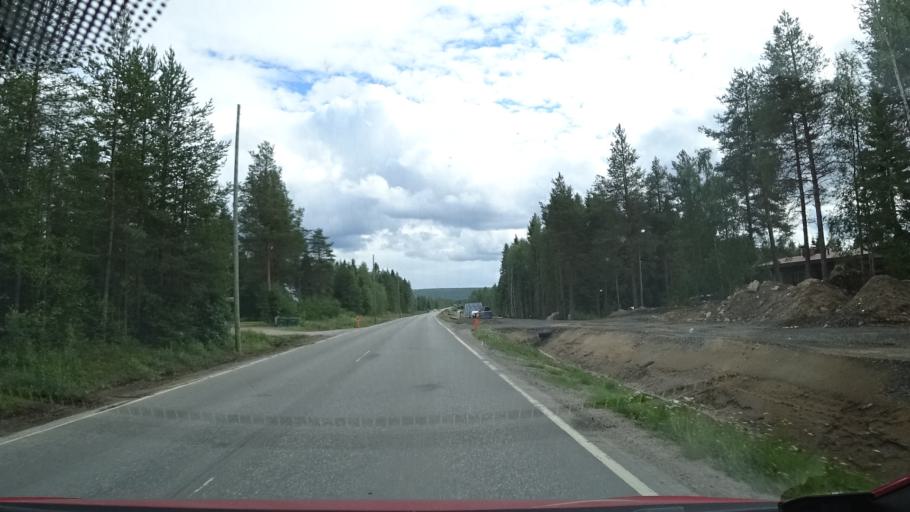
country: FI
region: Lapland
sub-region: Rovaniemi
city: Rovaniemi
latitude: 66.5329
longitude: 25.7334
